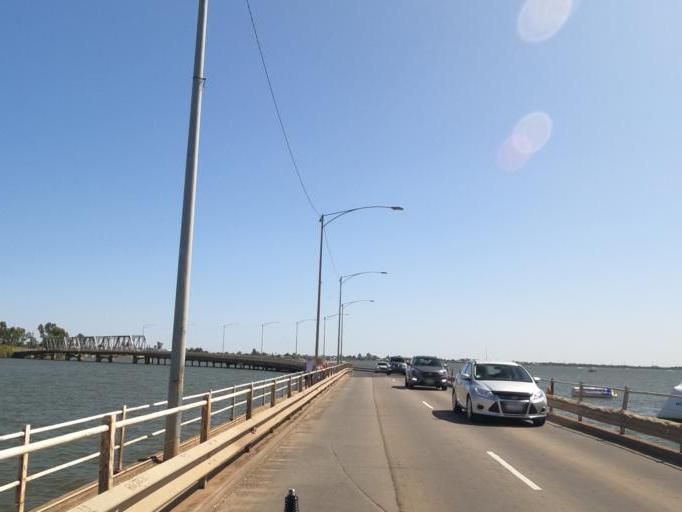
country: AU
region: Victoria
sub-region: Moira
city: Yarrawonga
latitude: -36.0072
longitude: 146.0049
